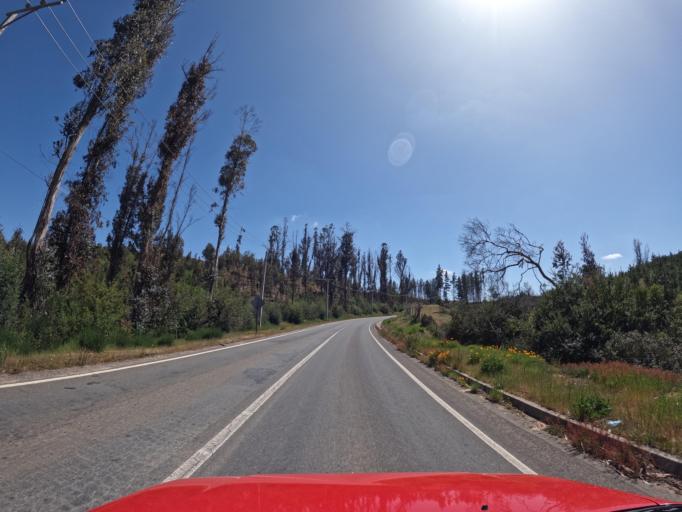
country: CL
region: O'Higgins
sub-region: Provincia de Colchagua
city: Santa Cruz
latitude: -34.6615
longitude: -71.8532
